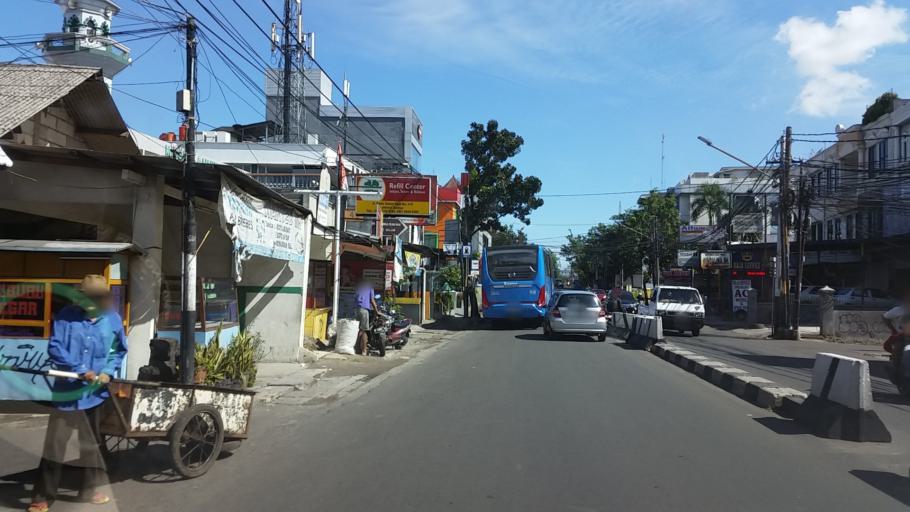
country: ID
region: Jakarta Raya
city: Jakarta
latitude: -6.2610
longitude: 106.7888
